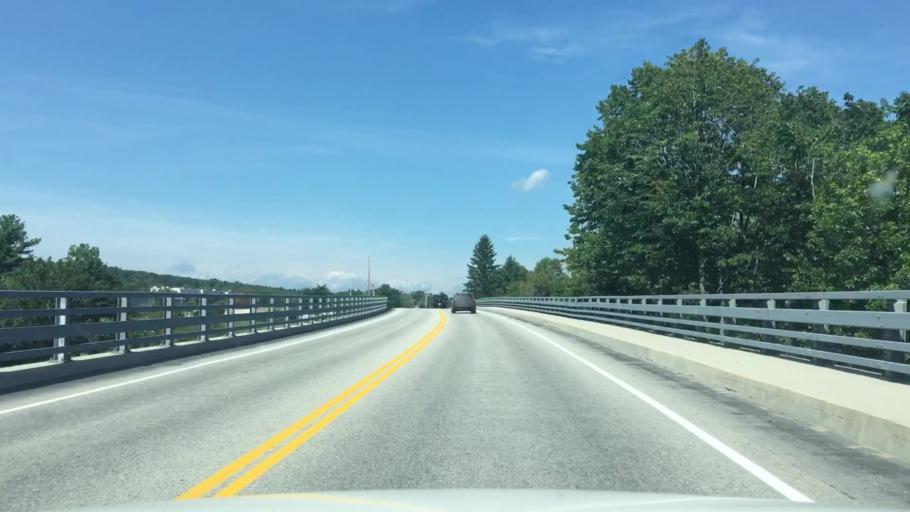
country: US
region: Maine
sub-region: Cumberland County
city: Falmouth
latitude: 43.7291
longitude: -70.2951
